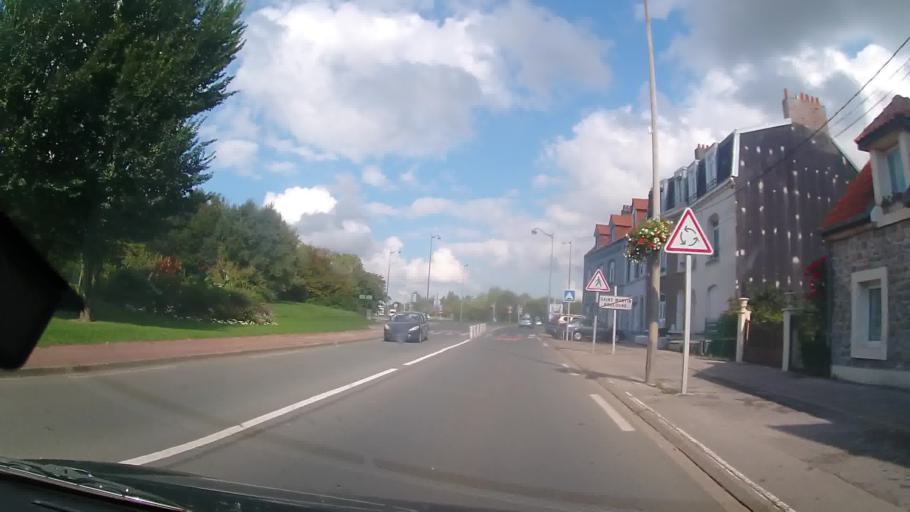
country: FR
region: Nord-Pas-de-Calais
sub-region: Departement du Pas-de-Calais
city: Saint-Martin-Boulogne
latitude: 50.7397
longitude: 1.6256
